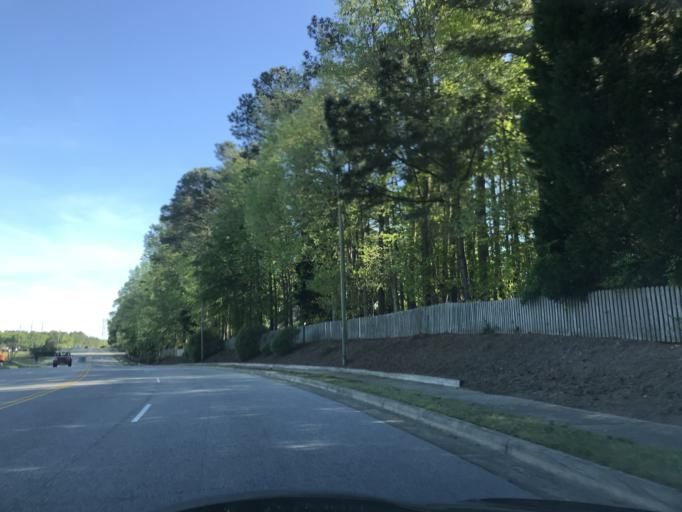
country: US
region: North Carolina
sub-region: Wake County
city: Knightdale
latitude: 35.8080
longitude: -78.5564
